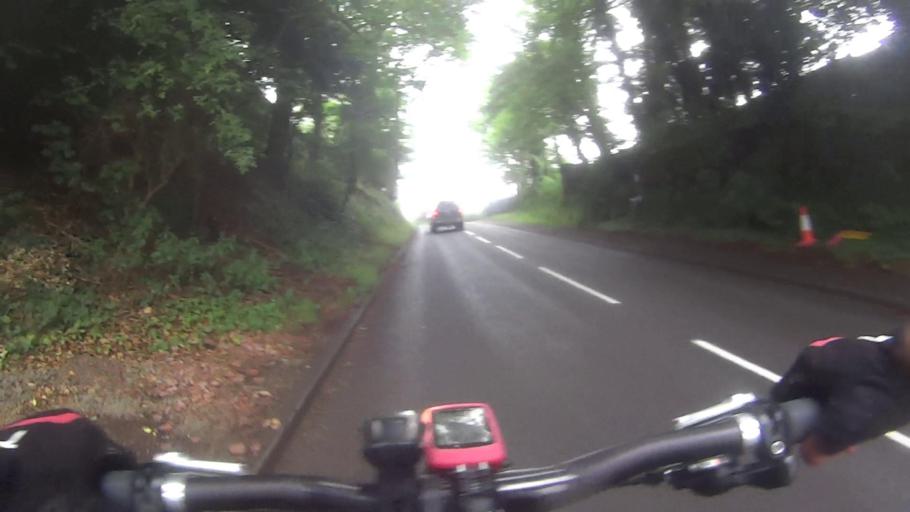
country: GB
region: England
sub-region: Worcestershire
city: Tenbury Wells
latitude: 52.3076
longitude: -2.5968
